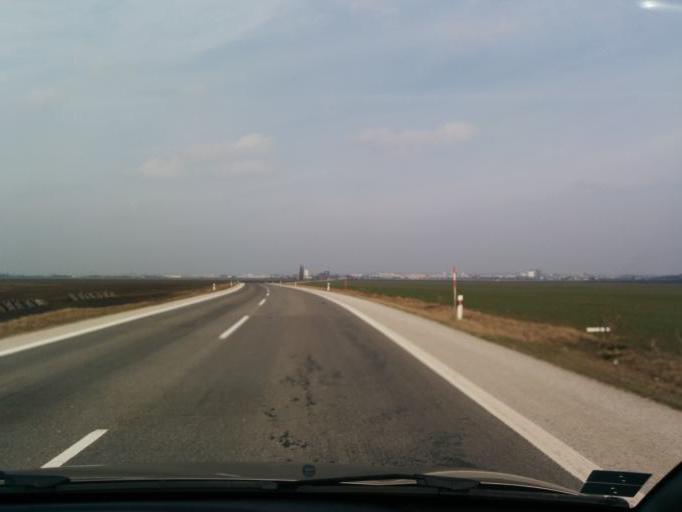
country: SK
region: Trnavsky
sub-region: Okres Galanta
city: Galanta
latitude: 48.2560
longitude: 17.7110
